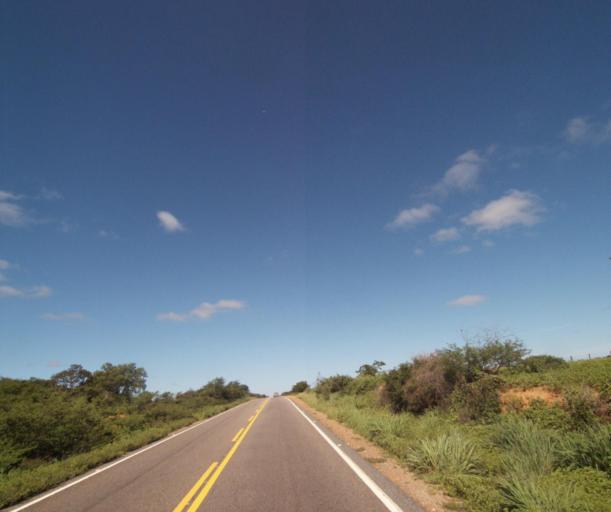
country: BR
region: Bahia
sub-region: Palmas De Monte Alto
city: Palmas de Monte Alto
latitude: -14.2436
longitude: -43.0894
